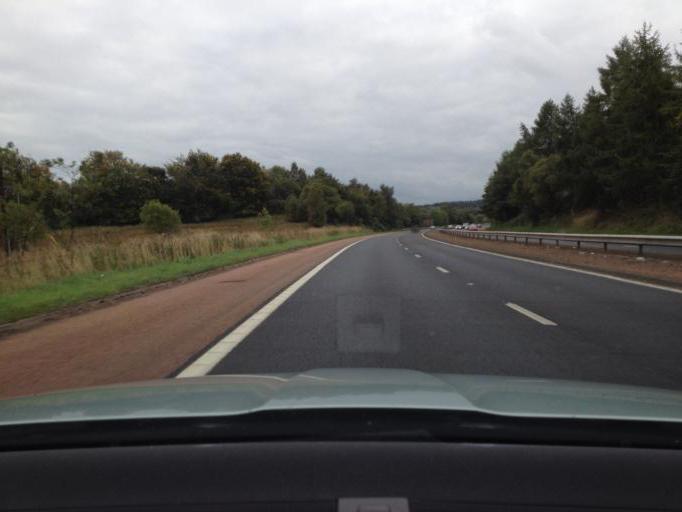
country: GB
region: Scotland
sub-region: Fife
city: Kelty
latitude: 56.1466
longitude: -3.3929
